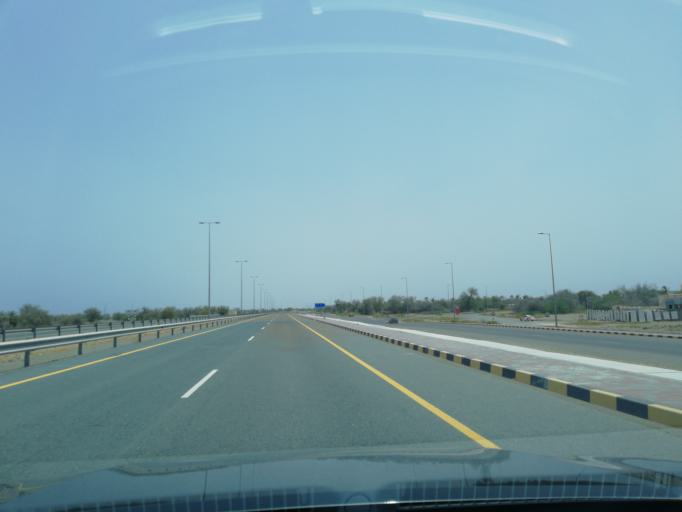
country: OM
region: Al Batinah
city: Shinas
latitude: 24.7622
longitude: 56.4614
